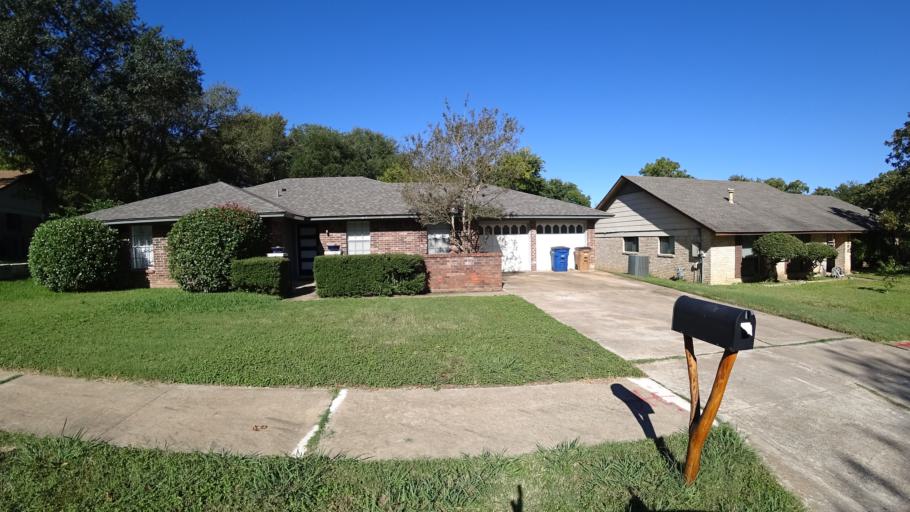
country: US
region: Texas
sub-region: Travis County
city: Rollingwood
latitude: 30.2180
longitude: -97.8115
